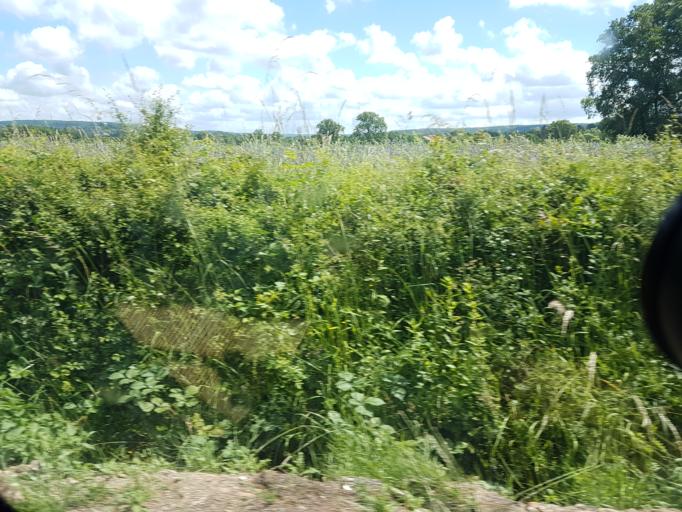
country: FR
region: Bourgogne
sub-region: Departement de Saone-et-Loire
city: Epinac
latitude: 46.9762
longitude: 4.4915
